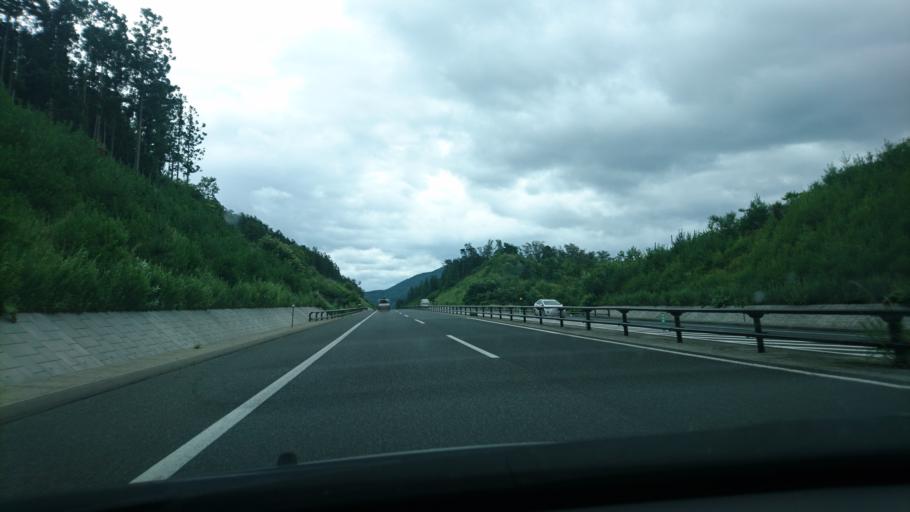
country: JP
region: Iwate
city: Ofunato
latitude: 39.0290
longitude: 141.6537
